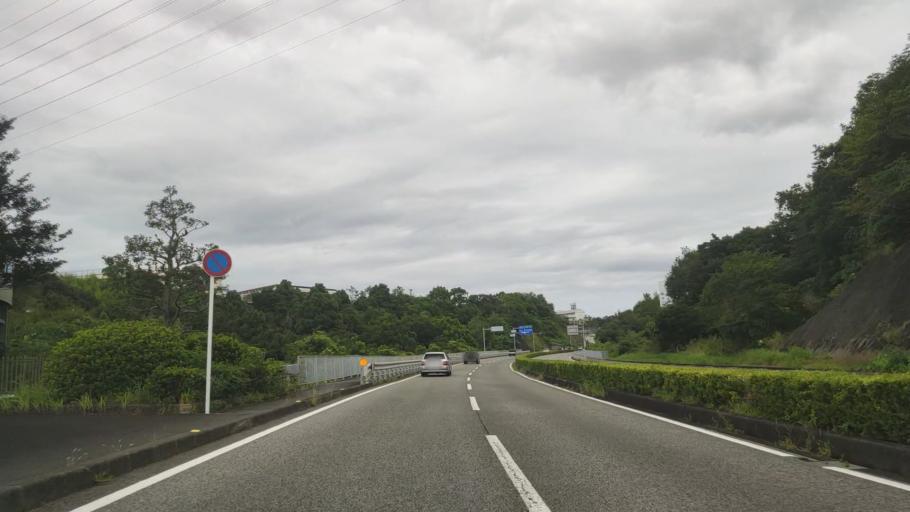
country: JP
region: Wakayama
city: Tanabe
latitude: 33.7289
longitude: 135.4008
